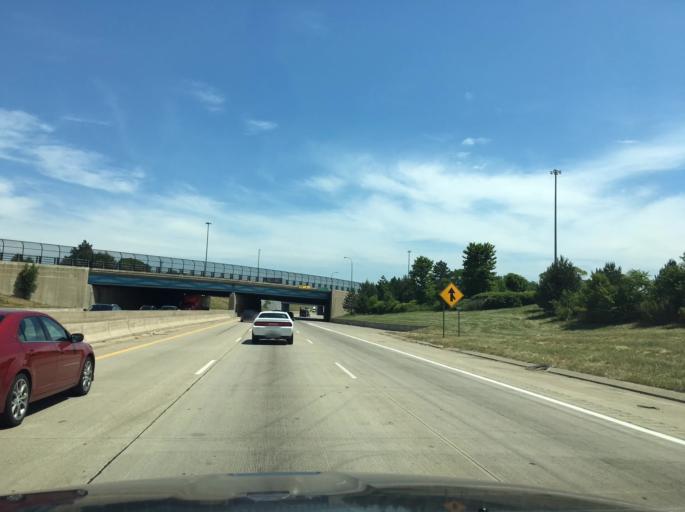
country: US
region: Michigan
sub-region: Wayne County
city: Dearborn
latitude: 42.3252
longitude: -83.1616
